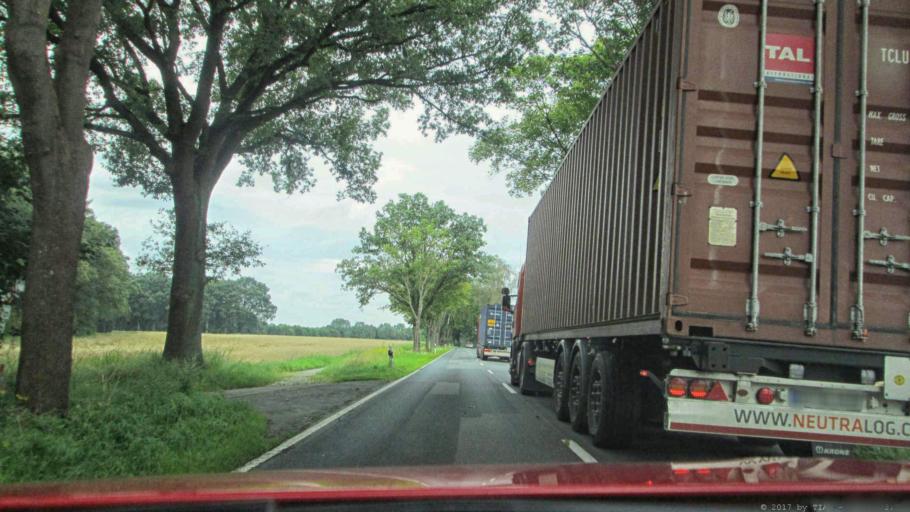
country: DE
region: Lower Saxony
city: Bodenteich
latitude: 52.8608
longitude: 10.6789
